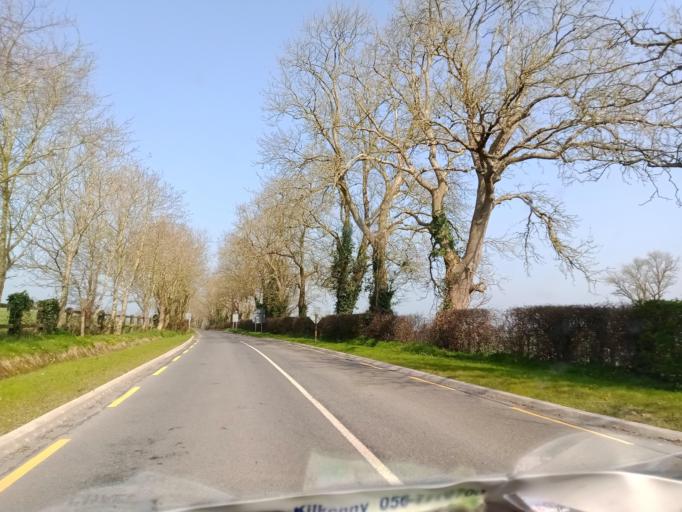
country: IE
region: Leinster
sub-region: Kilkenny
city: Callan
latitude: 52.5002
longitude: -7.3810
